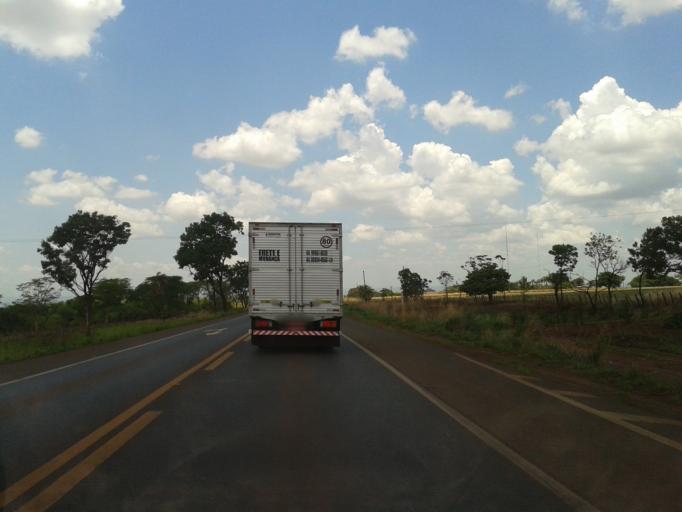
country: BR
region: Goias
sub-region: Itumbiara
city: Itumbiara
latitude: -18.3892
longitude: -49.3380
